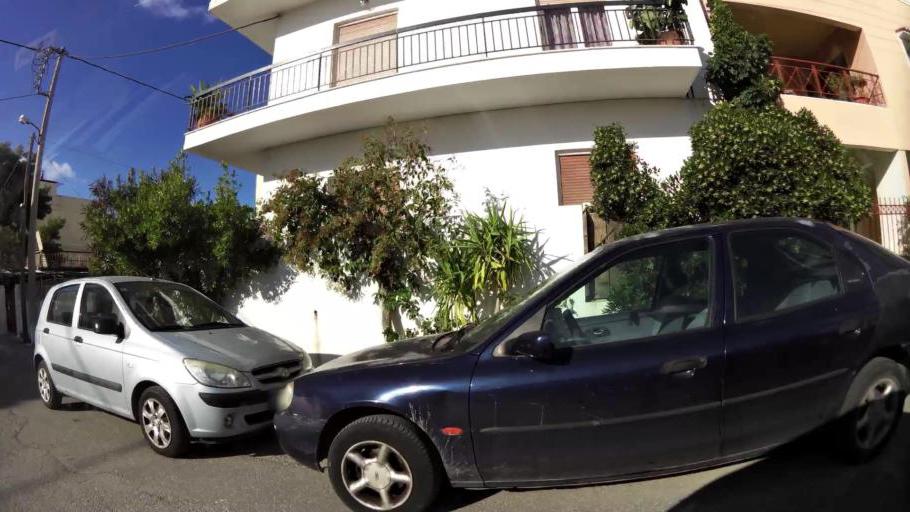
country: GR
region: Attica
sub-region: Nomarchia Anatolikis Attikis
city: Acharnes
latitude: 38.0680
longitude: 23.7415
